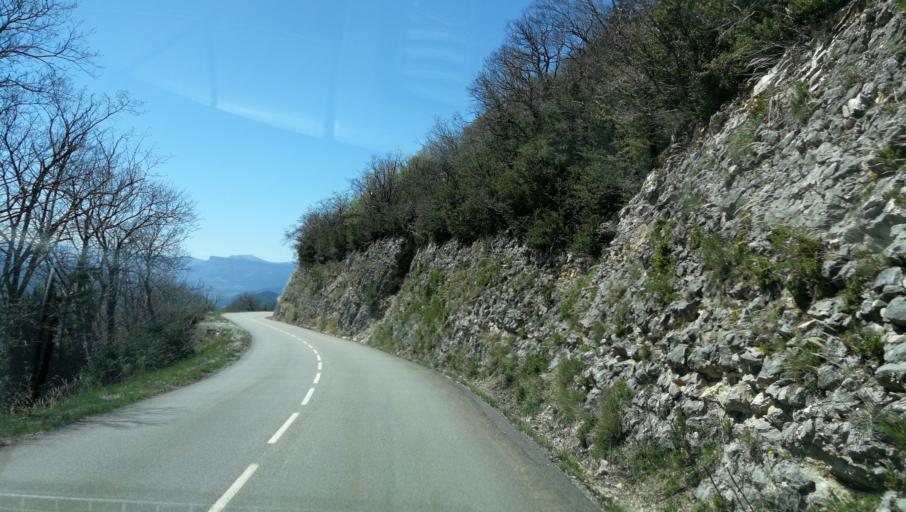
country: FR
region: Rhone-Alpes
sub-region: Departement de la Drome
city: Die
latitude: 44.8296
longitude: 5.3904
